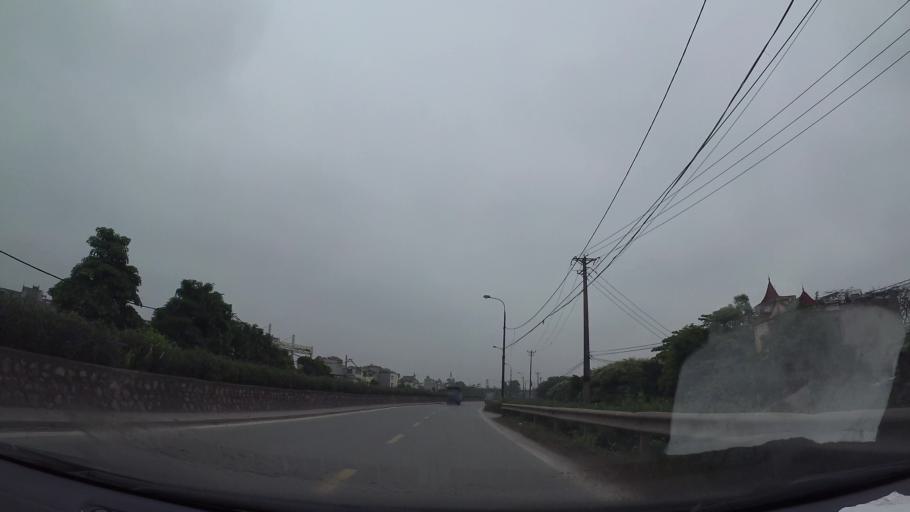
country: VN
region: Ha Noi
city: Hai BaTrung
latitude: 20.9907
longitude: 105.8932
